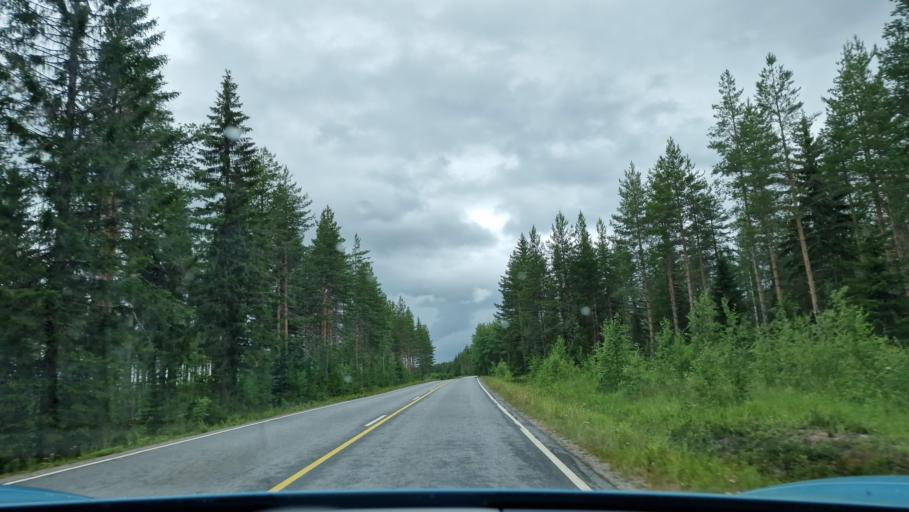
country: FI
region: Southern Ostrobothnia
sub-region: Jaerviseutu
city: Soini
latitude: 62.7537
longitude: 24.3981
